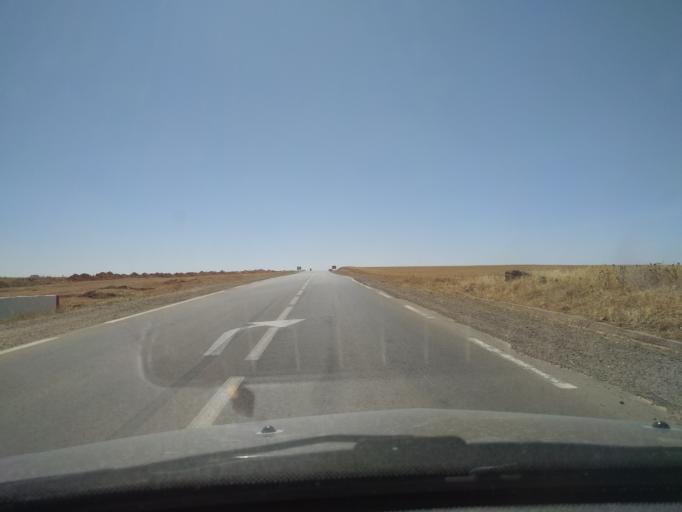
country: DZ
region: Tiaret
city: Frenda
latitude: 34.8949
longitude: 1.1682
